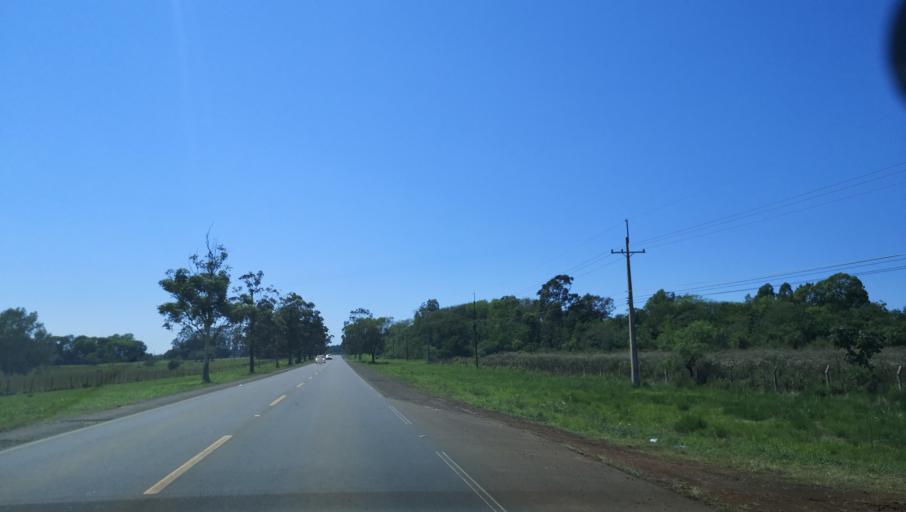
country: PY
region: Itapua
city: Carmen del Parana
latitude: -27.2214
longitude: -56.1156
